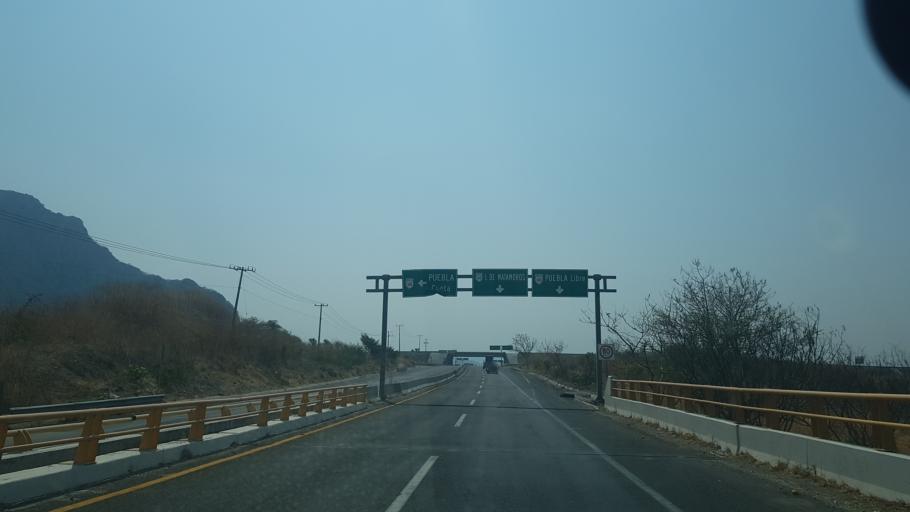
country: MX
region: Morelos
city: Jantetelco
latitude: 18.7047
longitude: -98.7719
